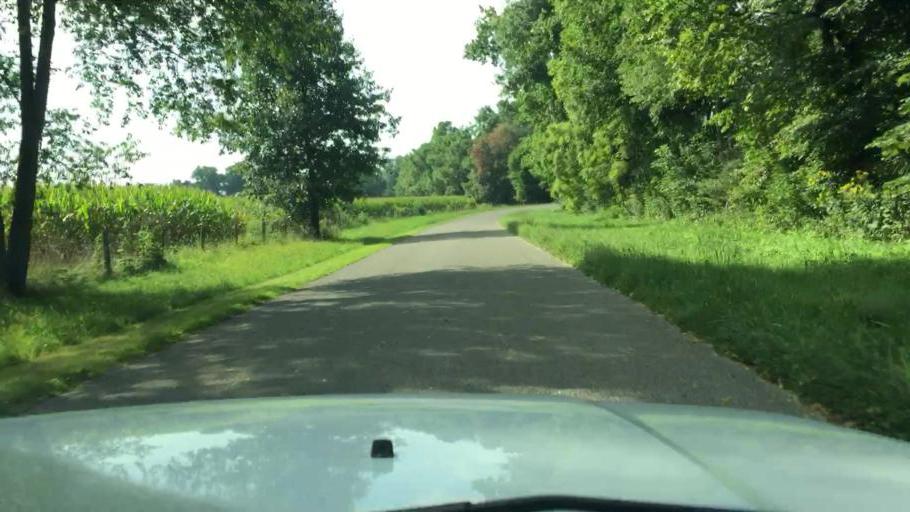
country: US
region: Ohio
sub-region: Champaign County
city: Mechanicsburg
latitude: 40.0646
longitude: -83.6017
